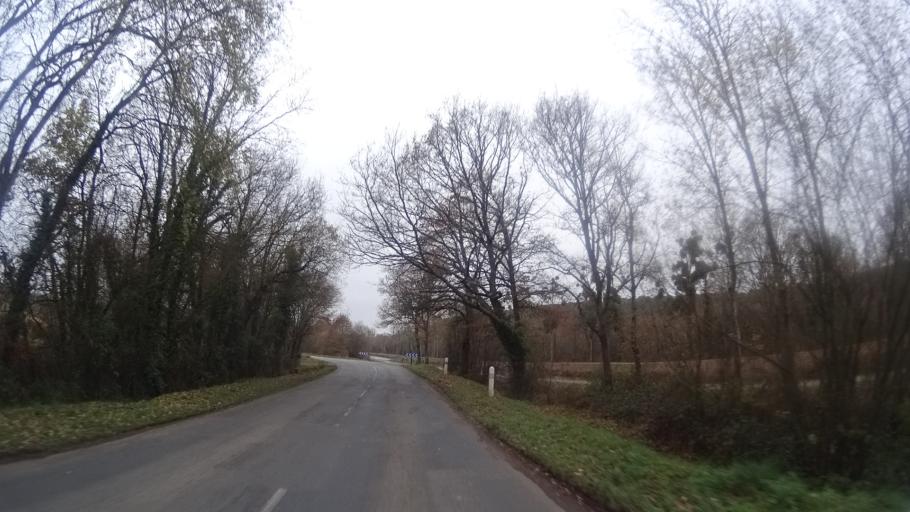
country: FR
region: Brittany
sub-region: Departement du Morbihan
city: Saint-Perreux
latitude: 47.6771
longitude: -2.0960
